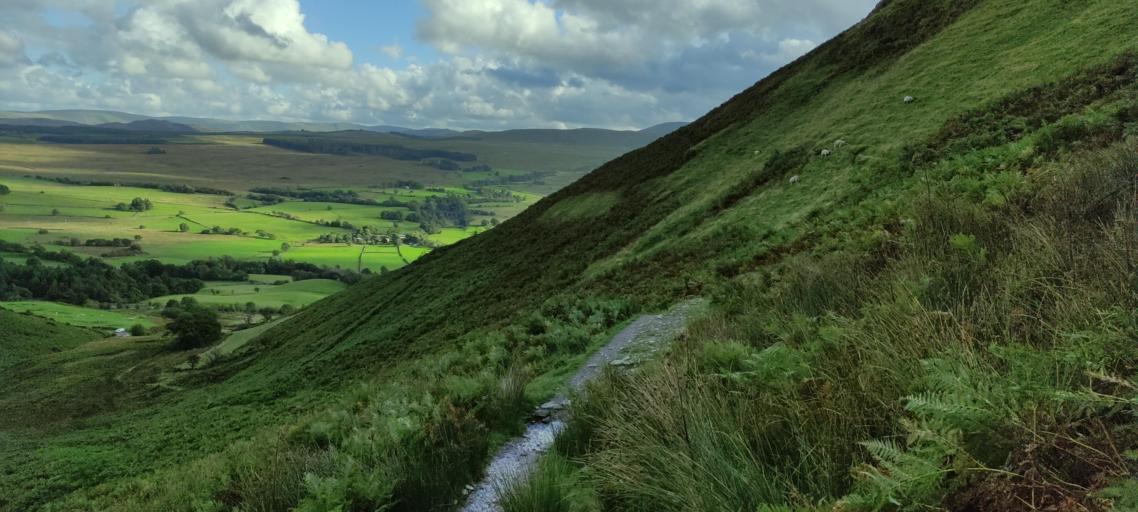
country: GB
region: England
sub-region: Cumbria
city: Keswick
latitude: 54.6389
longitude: -3.0160
